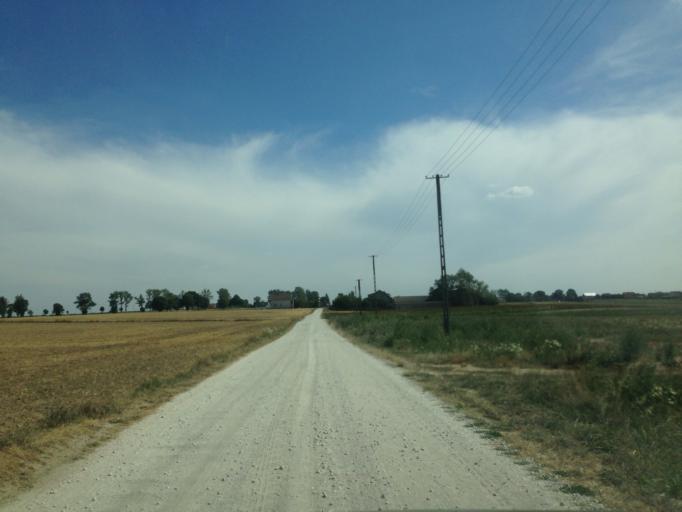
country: PL
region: Kujawsko-Pomorskie
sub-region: Powiat brodnicki
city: Bartniczka
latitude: 53.2320
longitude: 19.5890
